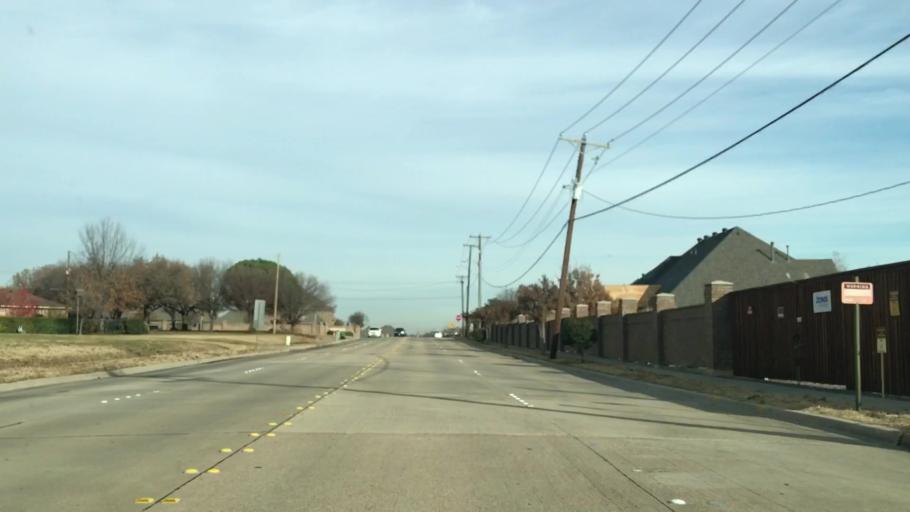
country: US
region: Texas
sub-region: Tarrant County
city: Watauga
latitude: 32.8917
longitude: -97.2119
